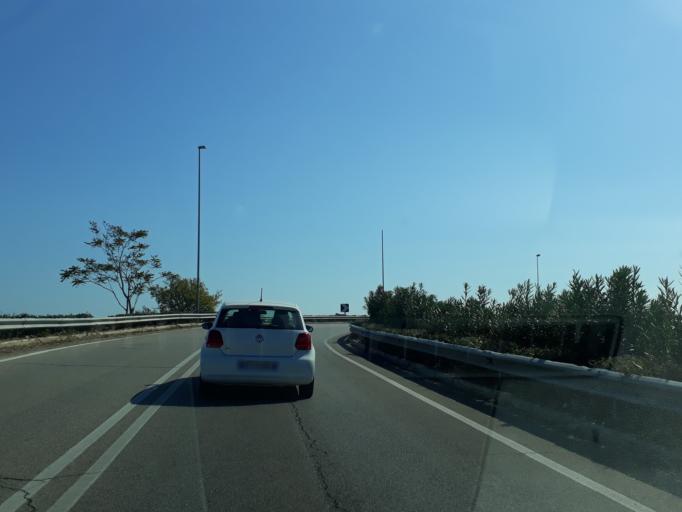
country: IT
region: Apulia
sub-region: Provincia di Bari
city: Monopoli
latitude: 40.9243
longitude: 17.3165
